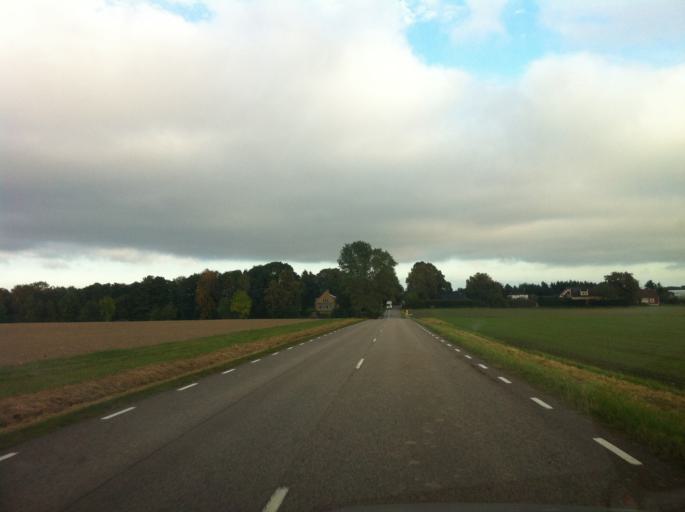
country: SE
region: Skane
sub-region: Helsingborg
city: Morarp
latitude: 56.0578
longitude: 12.8180
